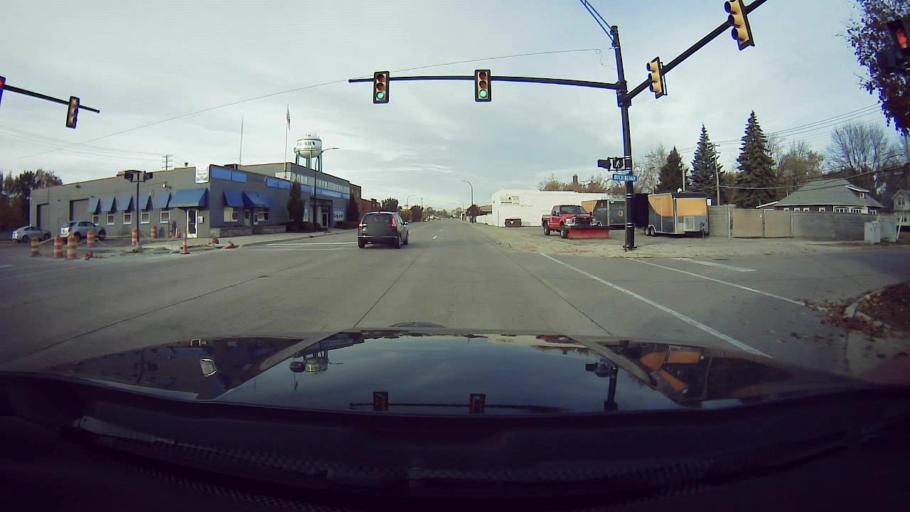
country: US
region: Michigan
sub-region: Oakland County
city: Berkley
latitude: 42.4887
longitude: -83.1921
